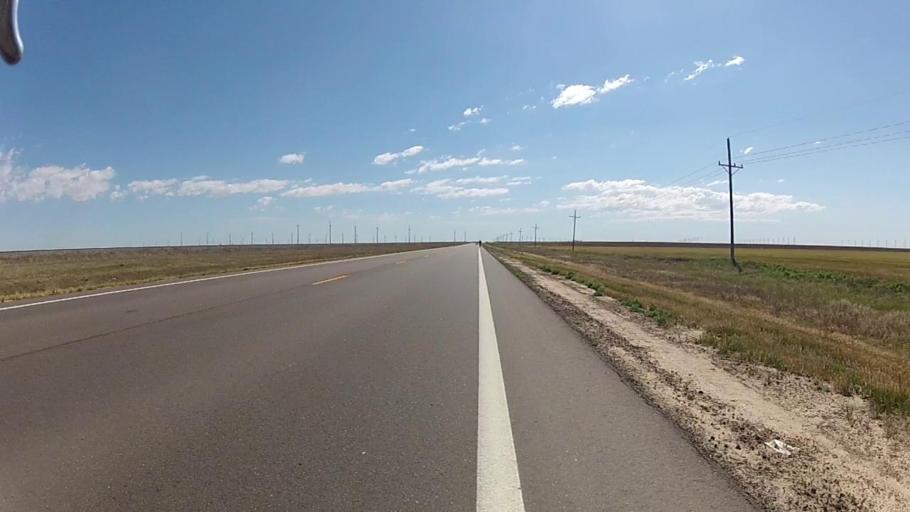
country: US
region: Kansas
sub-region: Gray County
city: Cimarron
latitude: 37.6034
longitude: -100.4275
